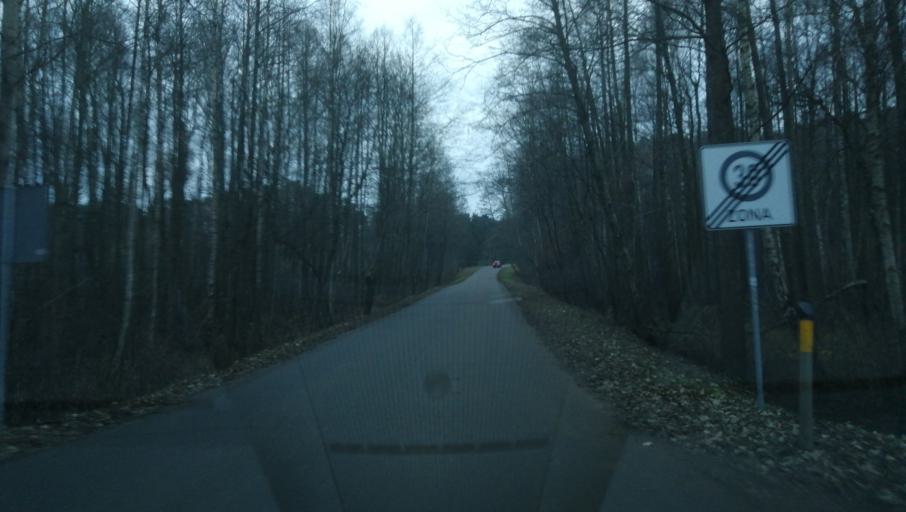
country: LV
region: Carnikava
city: Carnikava
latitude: 57.1464
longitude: 24.2928
